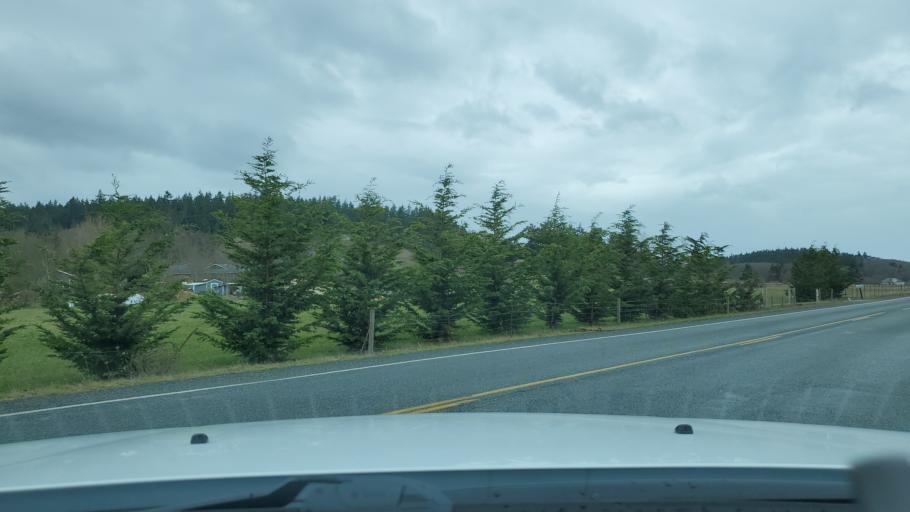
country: US
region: Washington
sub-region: Island County
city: Ault Field
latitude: 48.3114
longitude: -122.6914
